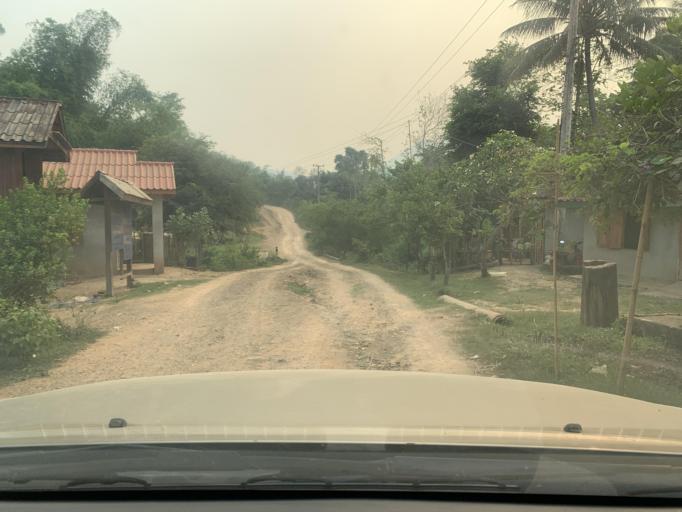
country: LA
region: Louangphabang
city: Louangphabang
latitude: 19.9289
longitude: 102.0782
